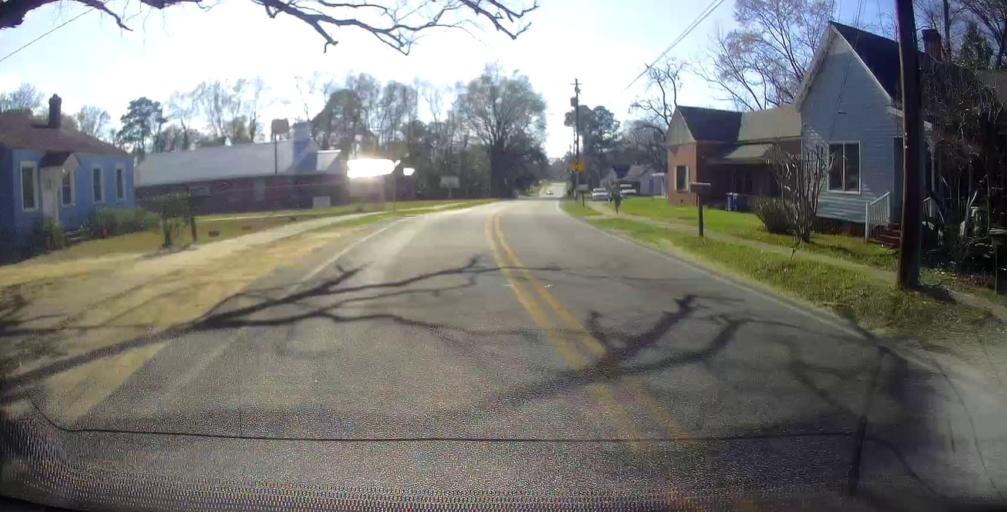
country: US
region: Georgia
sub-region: Laurens County
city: Dublin
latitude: 32.5427
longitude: -82.9127
